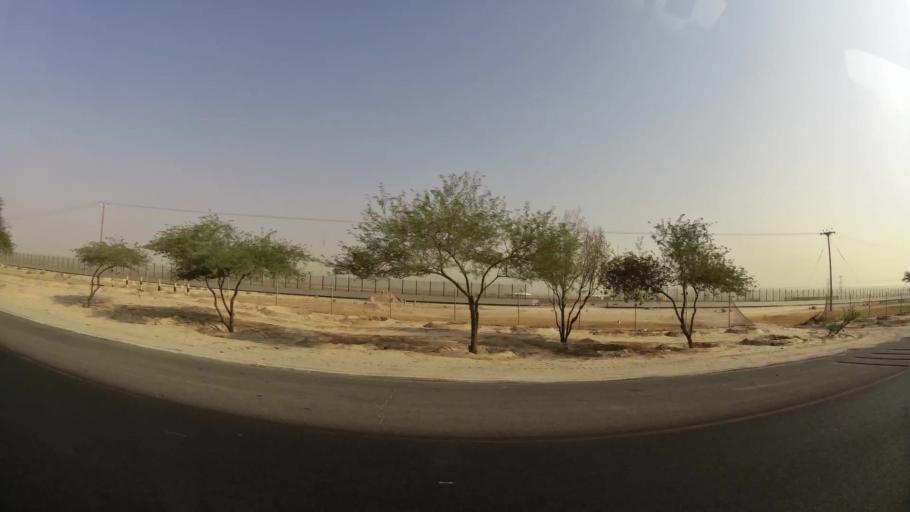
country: KW
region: Mubarak al Kabir
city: Mubarak al Kabir
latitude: 29.1742
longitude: 48.0395
